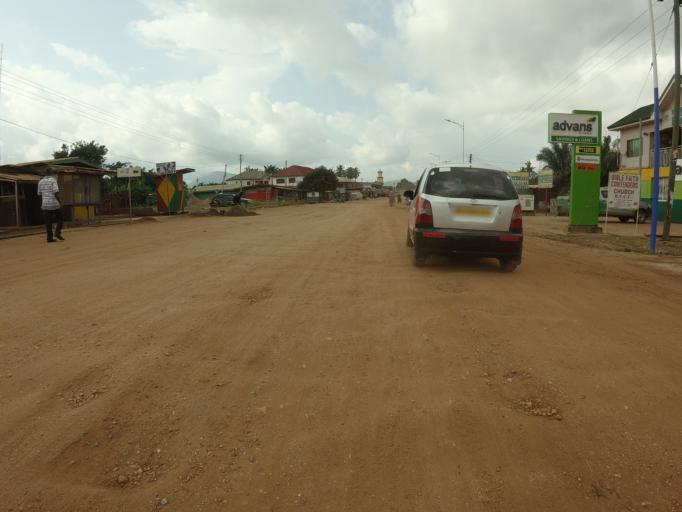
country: GH
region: Volta
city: Hohoe
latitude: 7.1479
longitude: 0.4669
